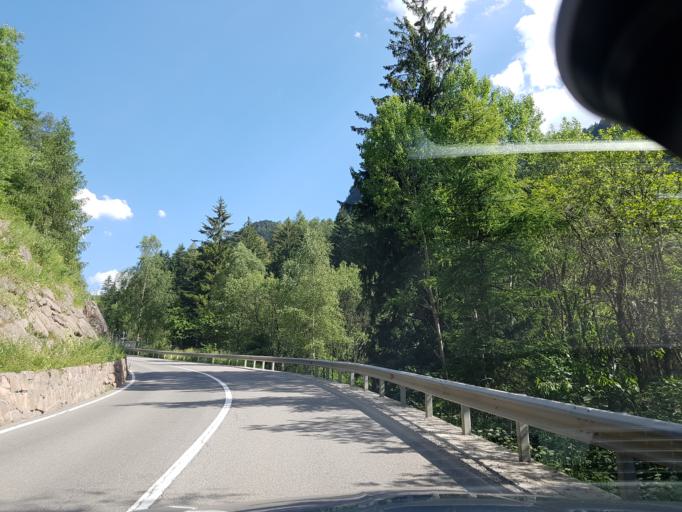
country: IT
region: Trentino-Alto Adige
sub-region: Bolzano
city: Ortisei
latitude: 46.5879
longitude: 11.6282
